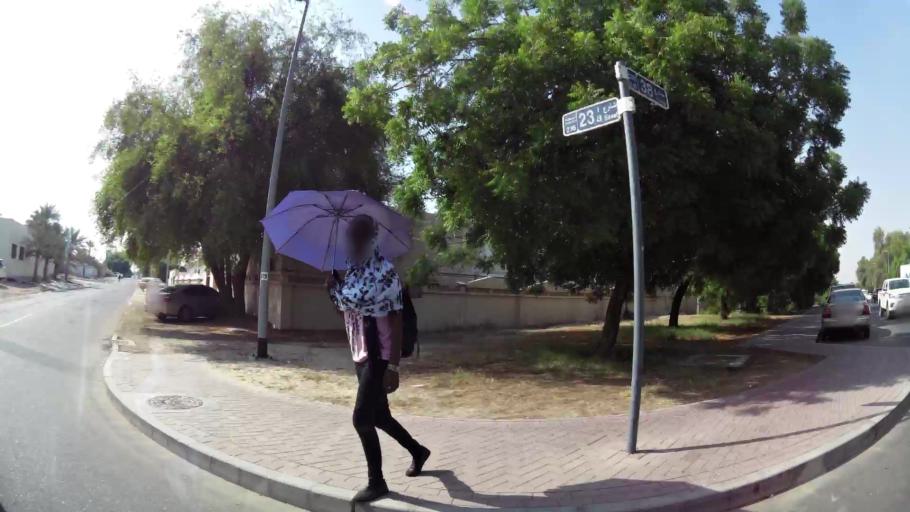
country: AE
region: Ash Shariqah
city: Sharjah
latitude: 25.2225
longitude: 55.3887
